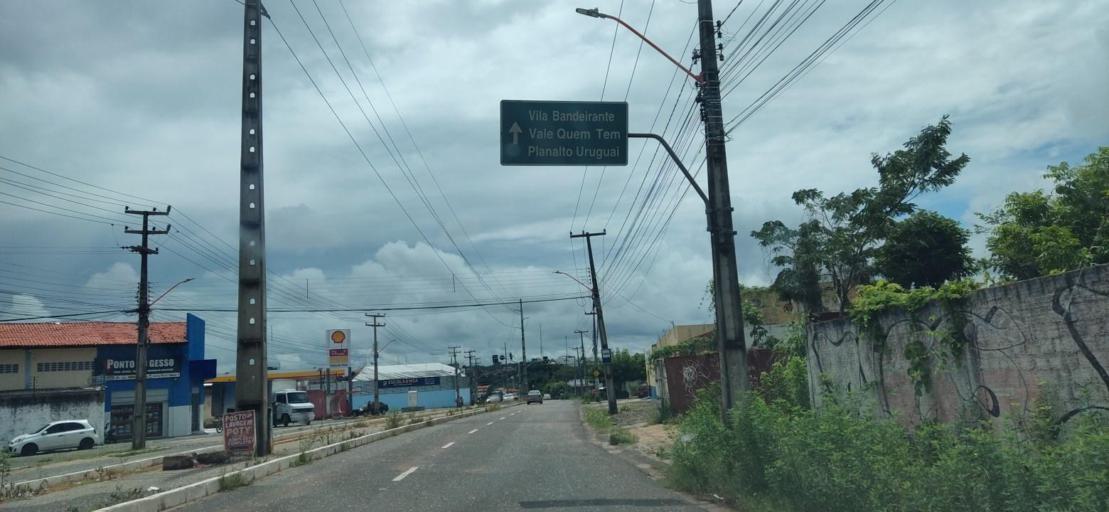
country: BR
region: Piaui
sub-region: Teresina
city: Teresina
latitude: -5.0626
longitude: -42.7579
